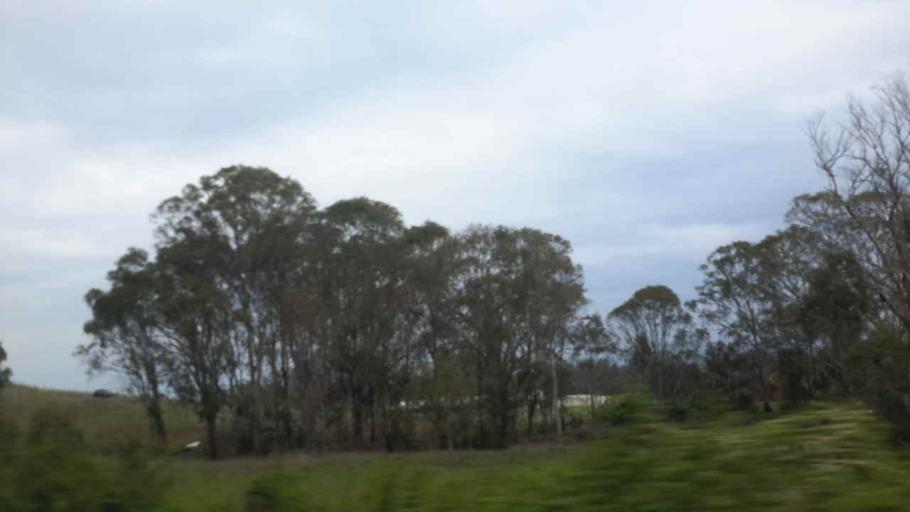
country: AU
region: New South Wales
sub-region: Penrith Municipality
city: Mulgoa
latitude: -33.8419
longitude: 150.6860
